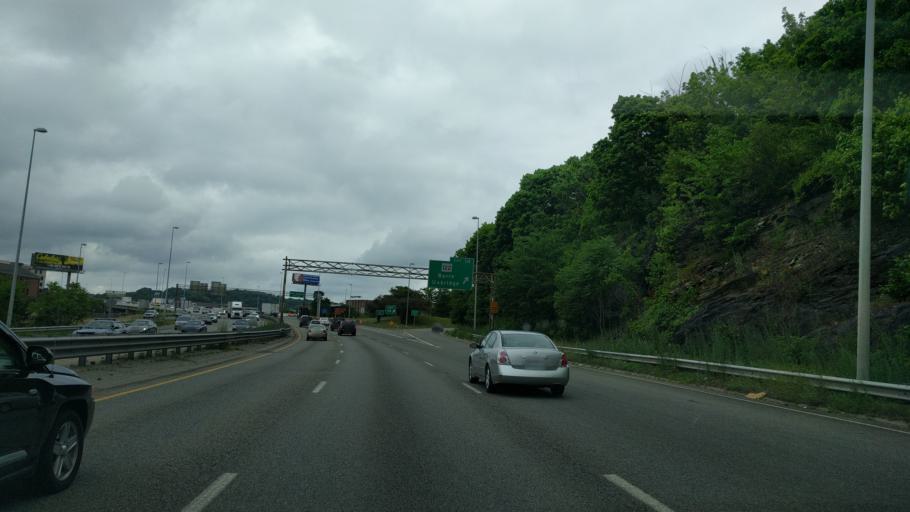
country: US
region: Massachusetts
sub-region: Worcester County
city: Worcester
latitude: 42.2561
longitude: -71.7948
